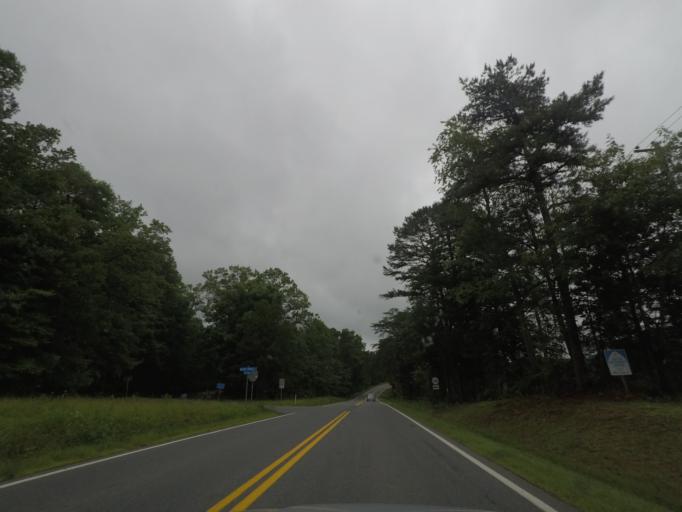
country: US
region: Virginia
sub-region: Fluvanna County
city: Palmyra
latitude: 37.9046
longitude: -78.2569
